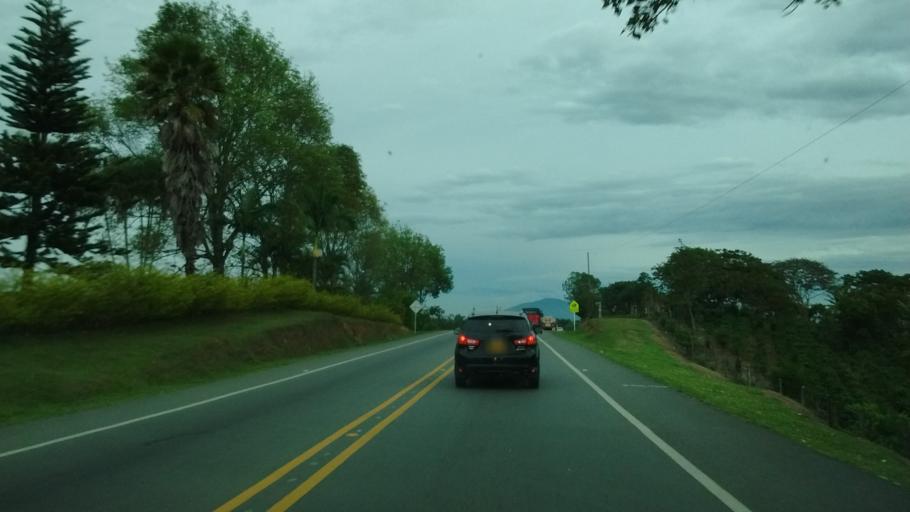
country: CO
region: Cauca
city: Morales
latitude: 2.7405
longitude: -76.5481
